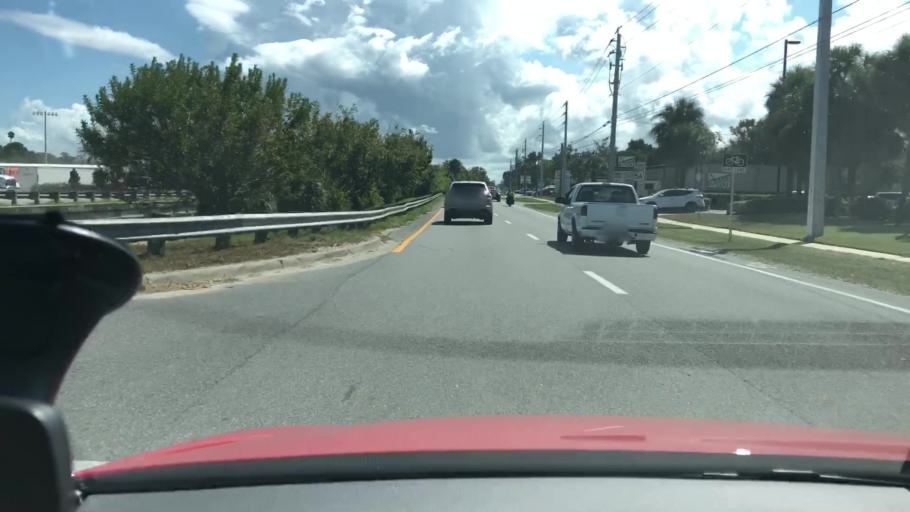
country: US
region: Florida
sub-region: Volusia County
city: South Daytona
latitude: 29.1543
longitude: -81.0198
